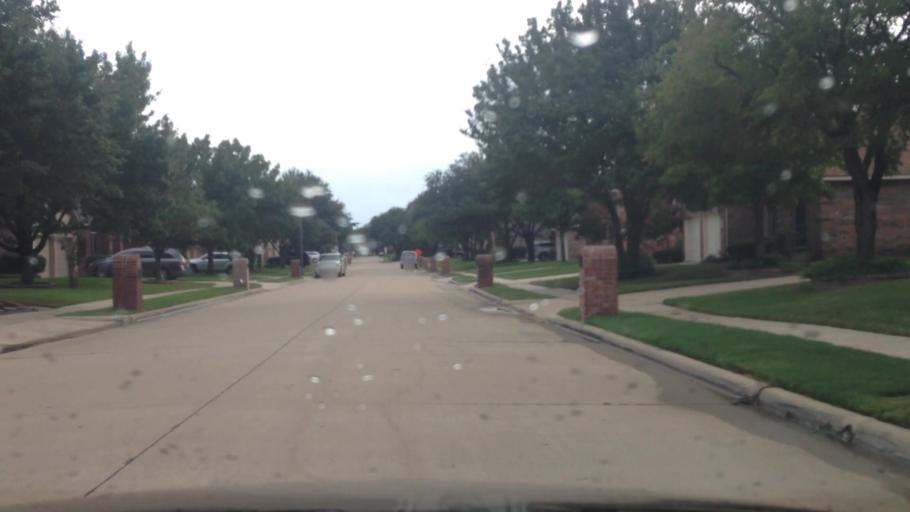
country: US
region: Texas
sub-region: Denton County
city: Flower Mound
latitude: 33.0209
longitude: -97.0486
